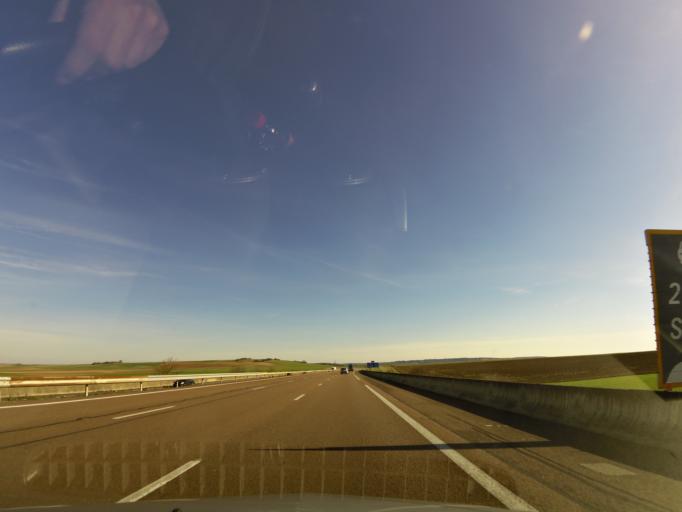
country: FR
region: Bourgogne
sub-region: Departement de l'Yonne
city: Aillant-sur-Tholon
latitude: 47.8960
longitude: 3.3950
